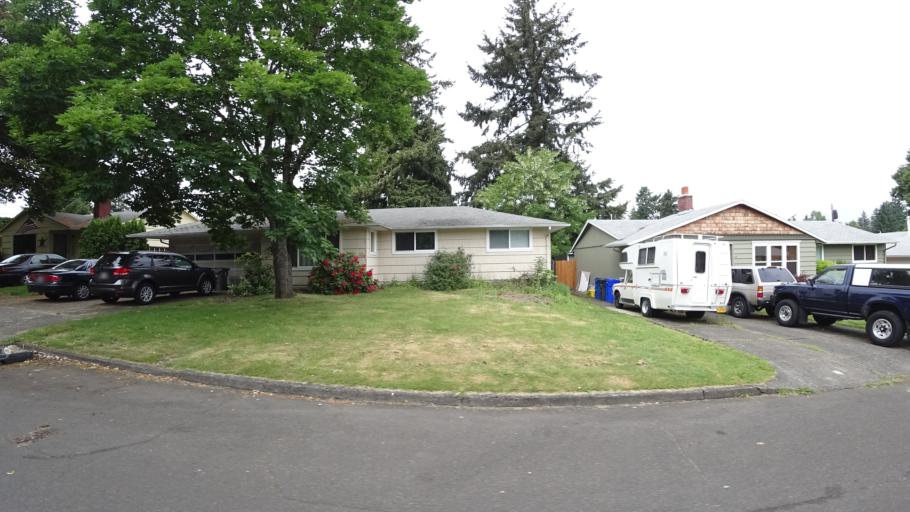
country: US
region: Oregon
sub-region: Multnomah County
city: Gresham
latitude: 45.4981
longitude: -122.4805
